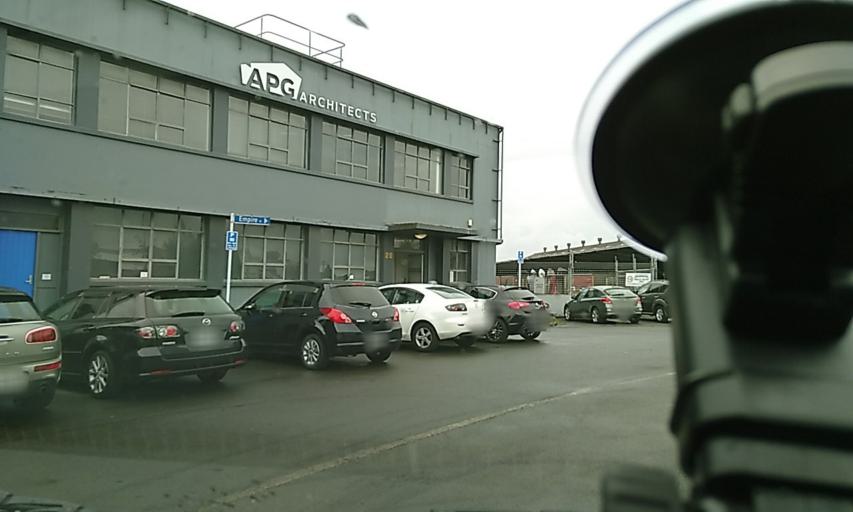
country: NZ
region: Waikato
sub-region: Hamilton City
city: Hamilton
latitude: -37.7869
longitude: 175.2614
